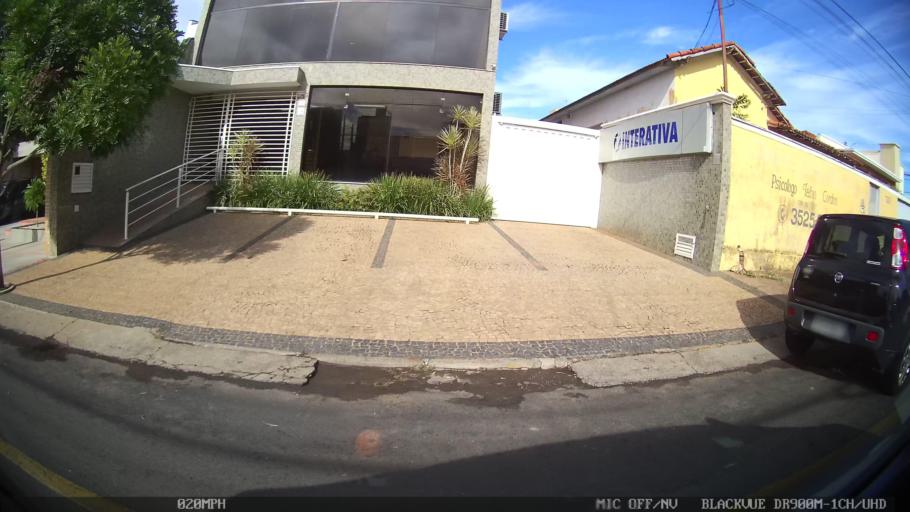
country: BR
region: Sao Paulo
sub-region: Catanduva
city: Catanduva
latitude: -21.1374
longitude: -48.9770
